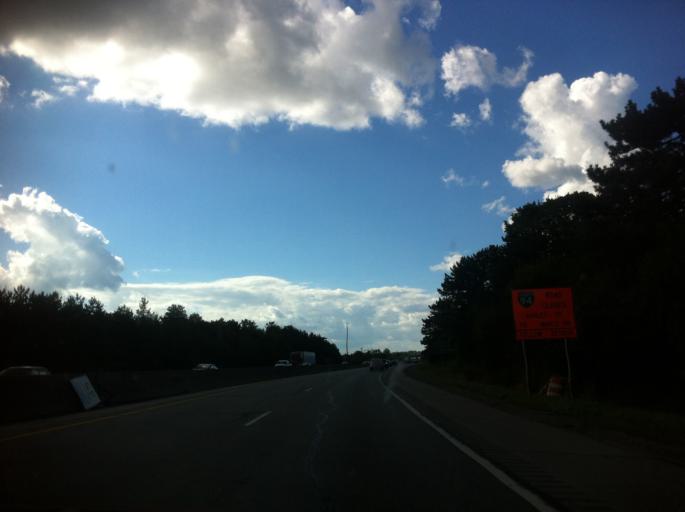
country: US
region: Michigan
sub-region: Washtenaw County
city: Ann Arbor
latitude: 42.2369
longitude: -83.7468
